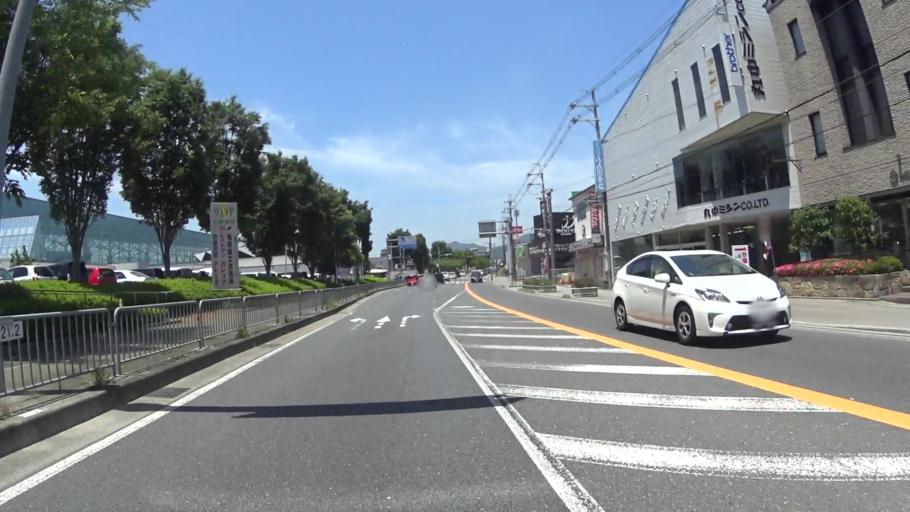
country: JP
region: Kyoto
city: Kameoka
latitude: 35.0148
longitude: 135.5684
